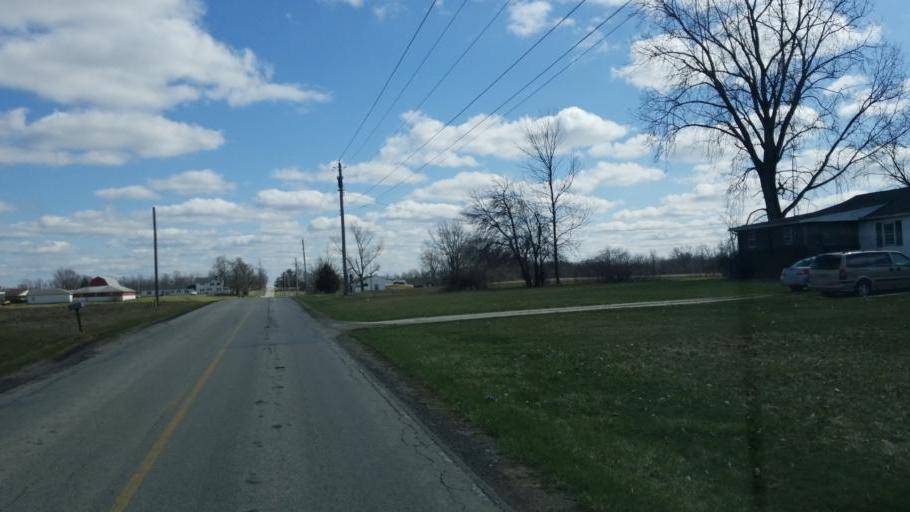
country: US
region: Ohio
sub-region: Richland County
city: Ontario
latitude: 40.8261
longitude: -82.5522
